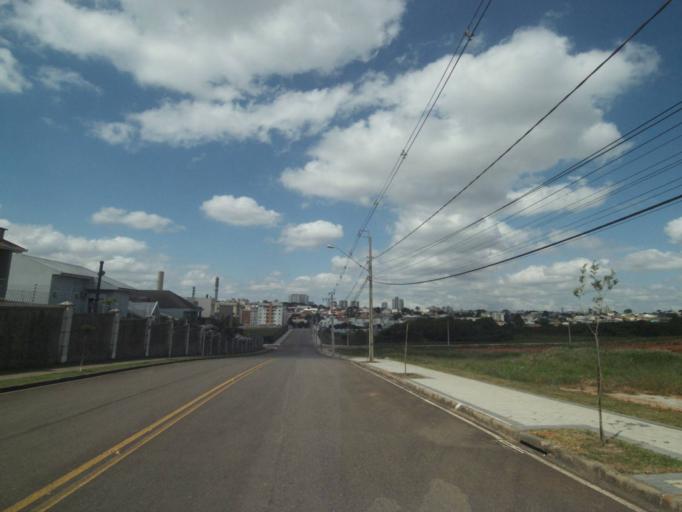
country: BR
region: Parana
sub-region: Curitiba
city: Curitiba
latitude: -25.5060
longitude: -49.3111
